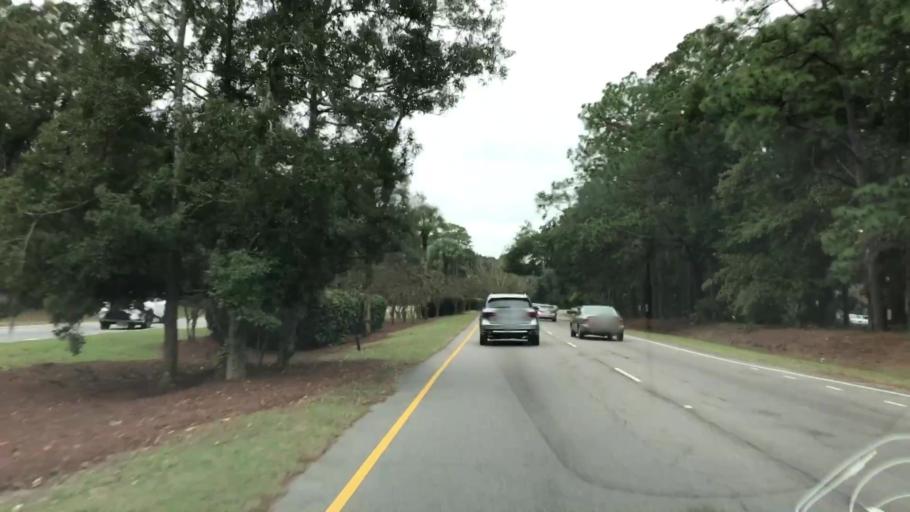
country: US
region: South Carolina
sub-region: Beaufort County
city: Hilton Head Island
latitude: 32.2142
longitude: -80.7220
